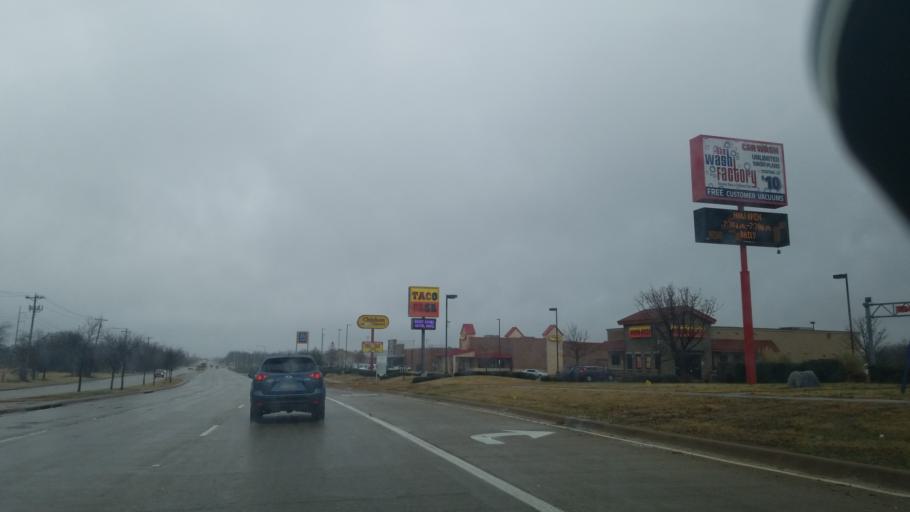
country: US
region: Texas
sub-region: Denton County
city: Denton
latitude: 33.1987
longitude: -97.0912
